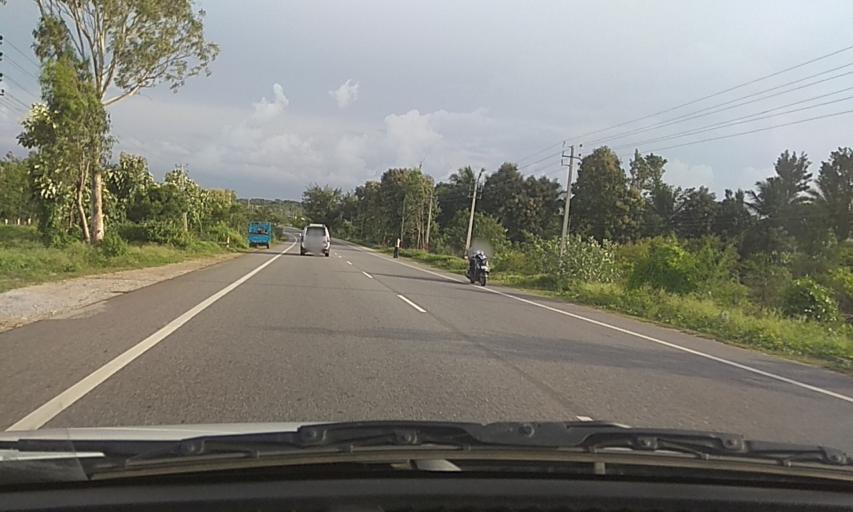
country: IN
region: Karnataka
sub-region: Mysore
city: Nanjangud
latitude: 12.0555
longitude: 76.6753
